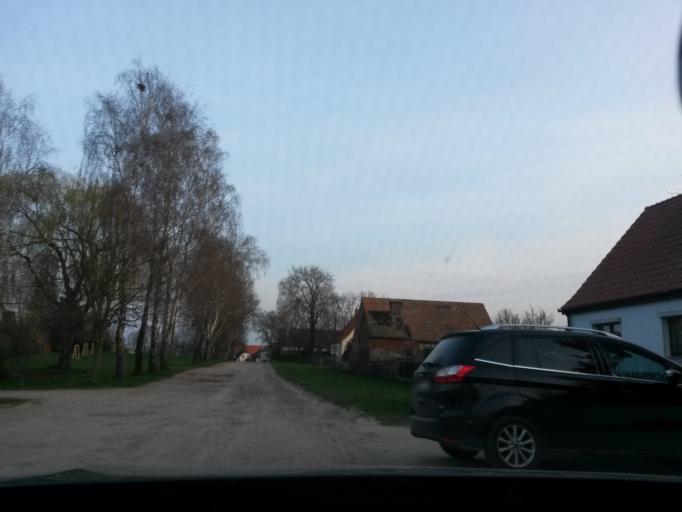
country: DE
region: Brandenburg
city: Protzel
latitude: 52.5700
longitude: 13.9670
